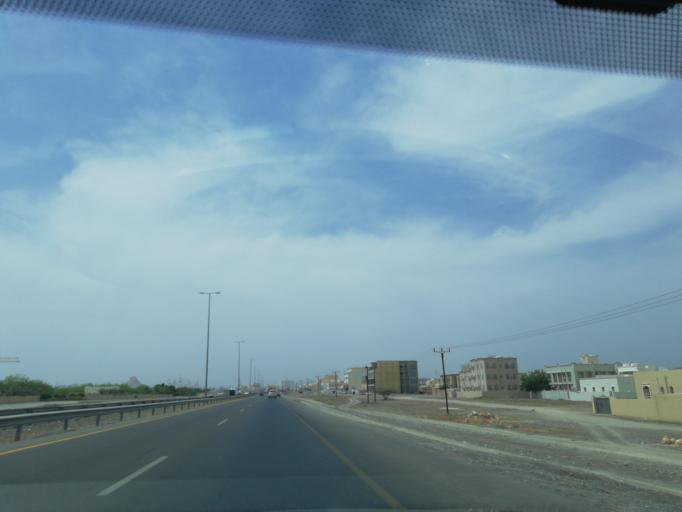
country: OM
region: Muhafazat ad Dakhiliyah
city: Nizwa
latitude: 22.8576
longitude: 57.5257
